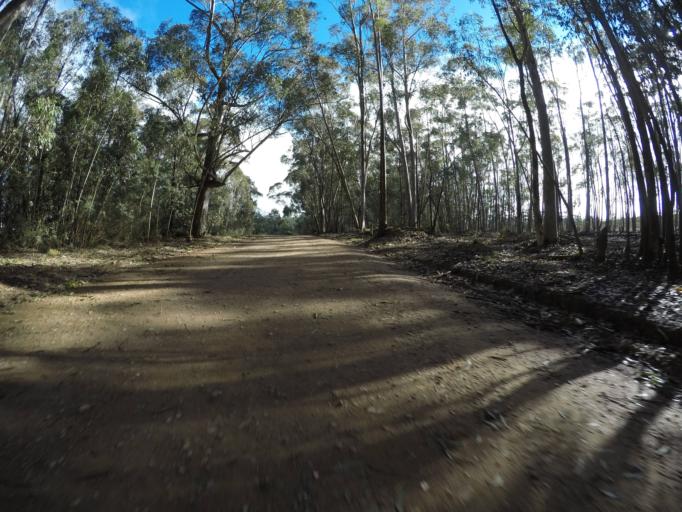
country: ZA
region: Western Cape
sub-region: Cape Winelands District Municipality
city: Ashton
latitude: -34.1122
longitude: 19.8000
